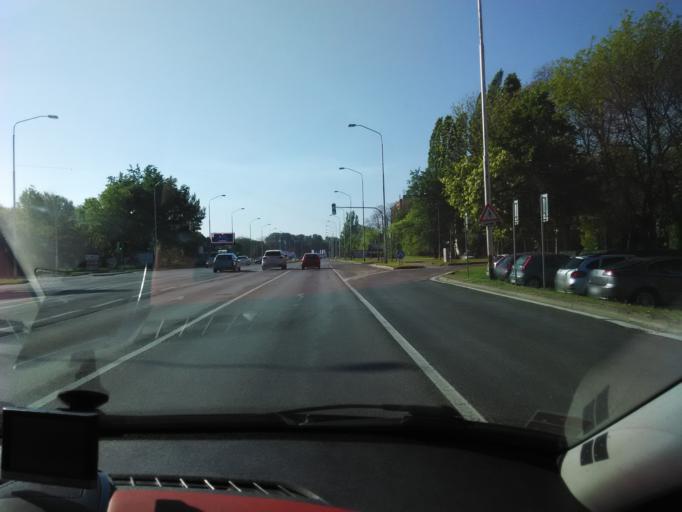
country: SK
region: Bratislavsky
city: Bratislava
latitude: 48.1247
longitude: 17.1317
